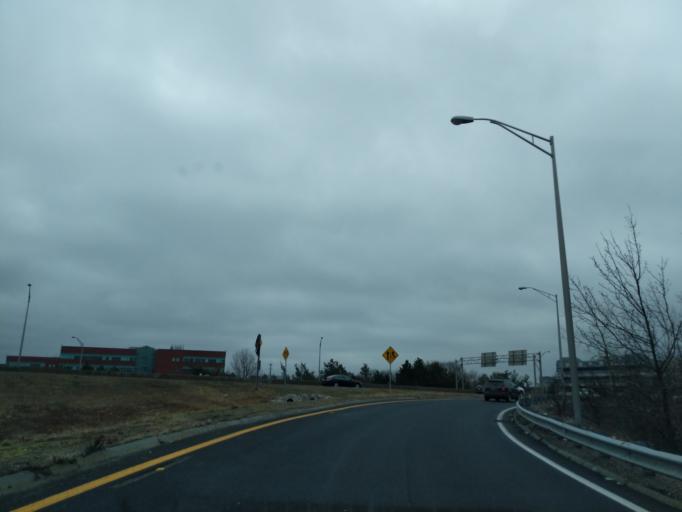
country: US
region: Massachusetts
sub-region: Middlesex County
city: Cochituate
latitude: 42.3124
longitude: -71.3858
